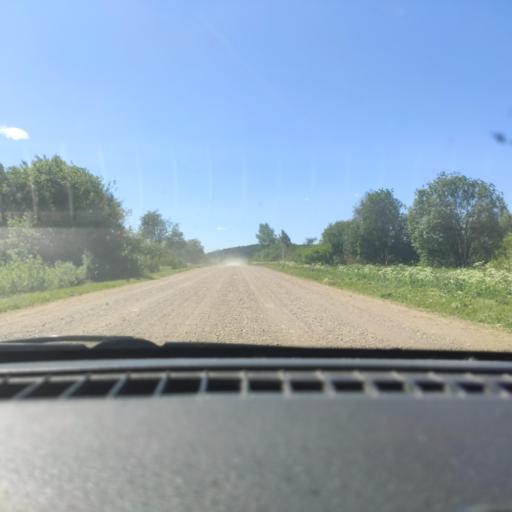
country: RU
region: Perm
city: Verkhnechusovskiye Gorodki
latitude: 58.1941
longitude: 57.1343
